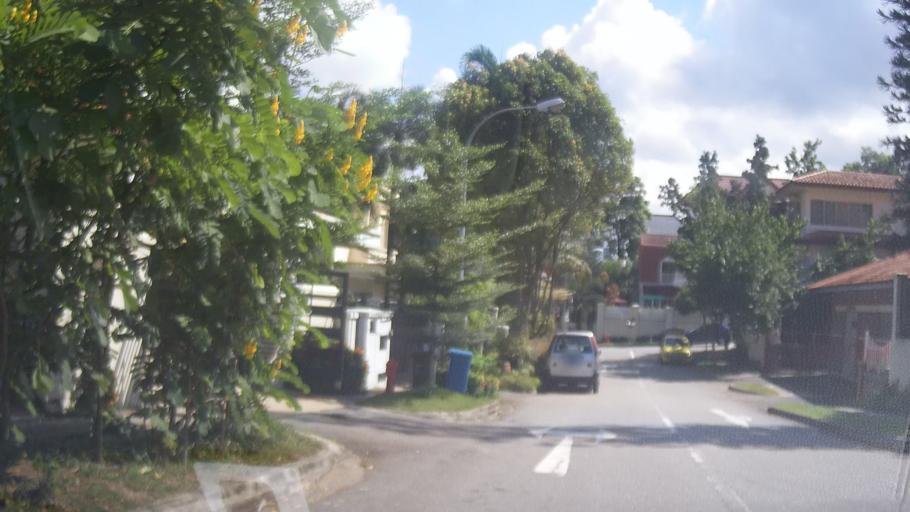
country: MY
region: Johor
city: Johor Bahru
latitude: 1.4270
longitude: 103.7777
